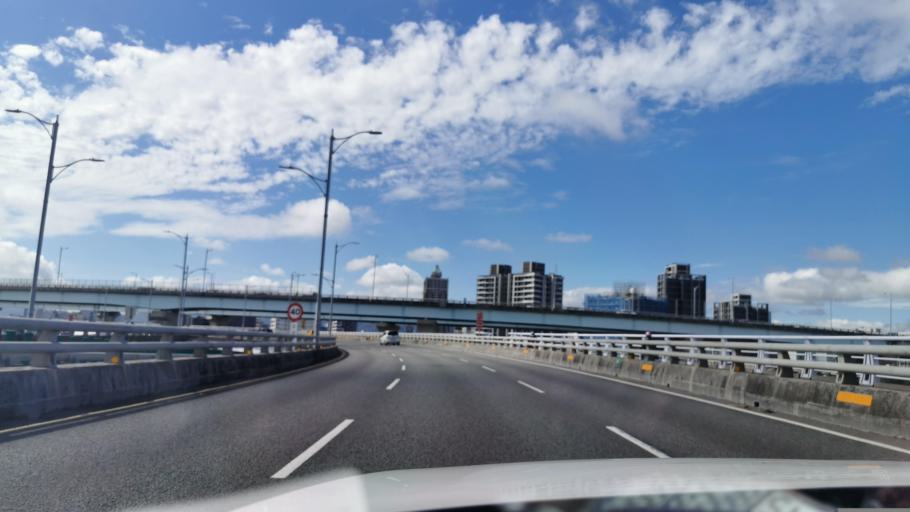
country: TW
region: Taipei
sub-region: Taipei
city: Banqiao
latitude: 25.0480
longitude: 121.4812
